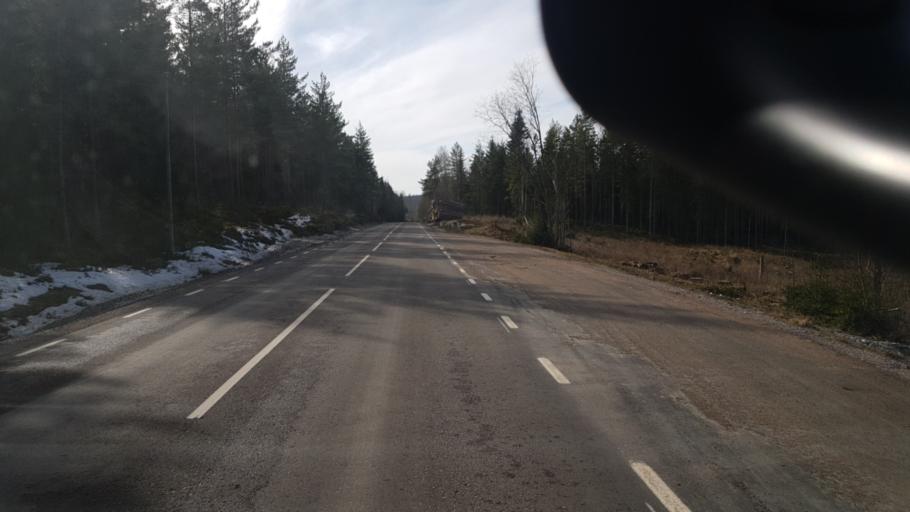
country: SE
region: Vaermland
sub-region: Eda Kommun
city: Amotfors
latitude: 59.7366
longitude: 12.4002
